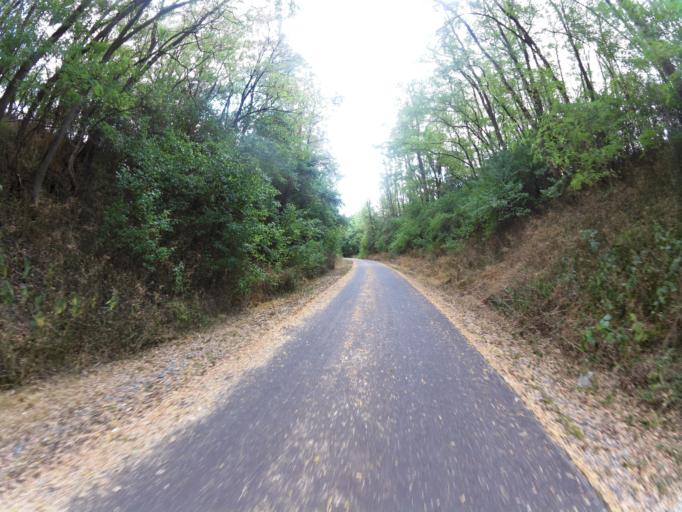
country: DE
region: Bavaria
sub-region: Regierungsbezirk Unterfranken
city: Sonderhofen
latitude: 49.5988
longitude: 10.0019
